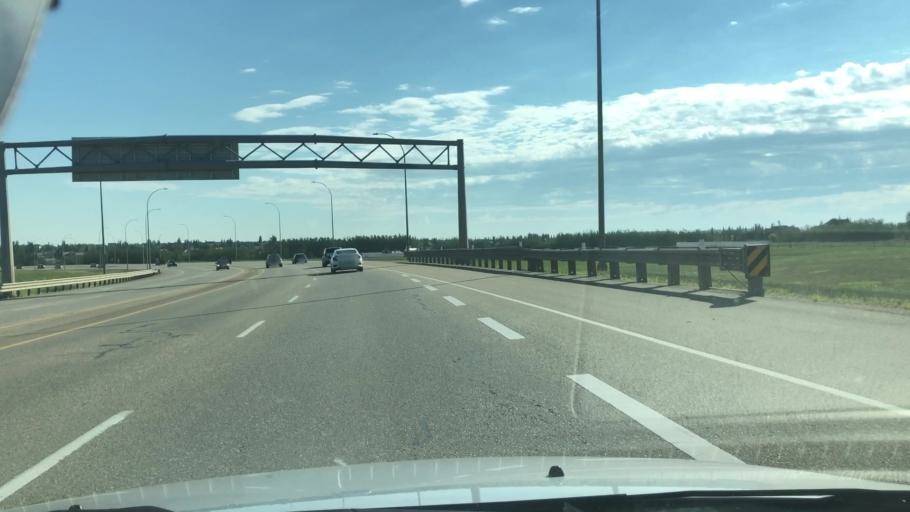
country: CA
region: Alberta
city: Devon
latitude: 53.4455
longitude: -113.5958
